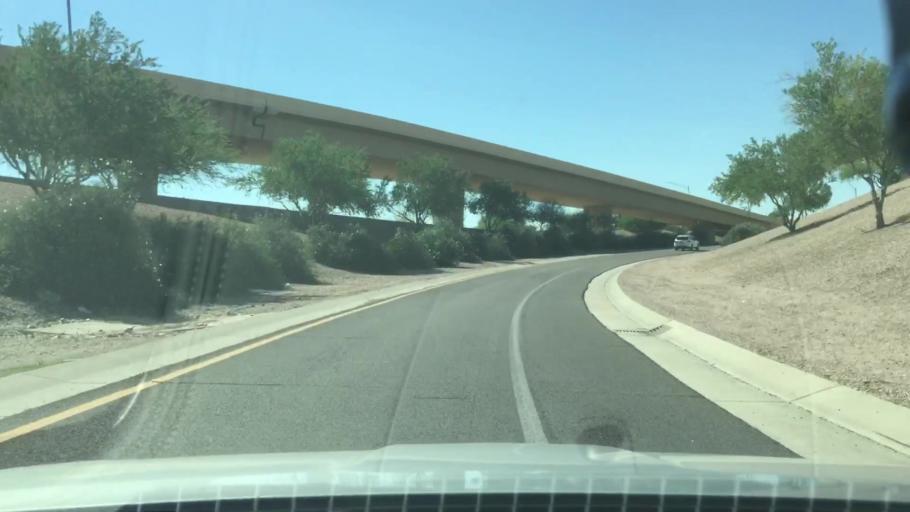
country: US
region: Arizona
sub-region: Maricopa County
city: Tempe
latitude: 33.3869
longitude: -111.8928
